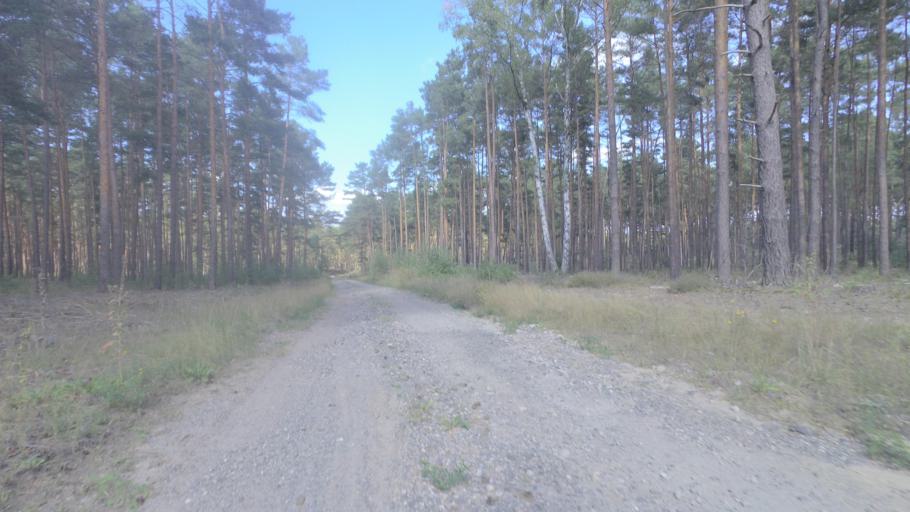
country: DE
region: Brandenburg
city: Munchehofe
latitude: 52.1824
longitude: 13.8720
